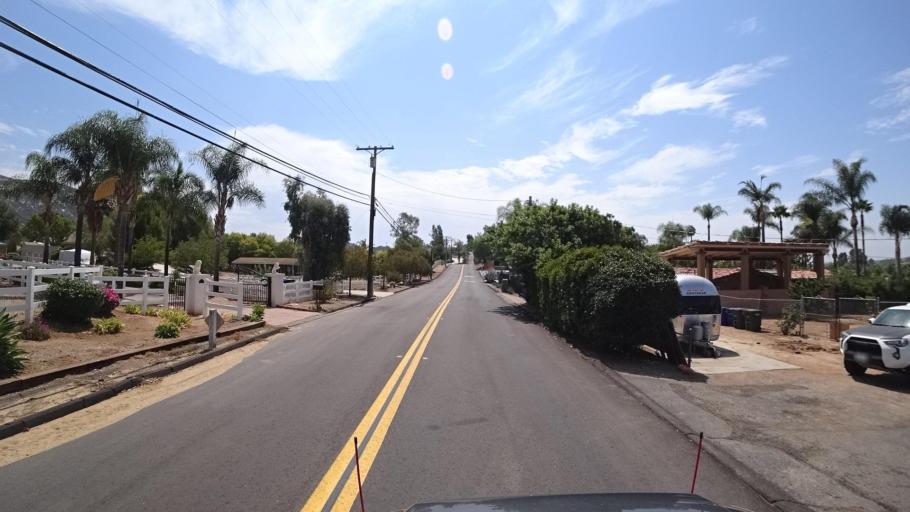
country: US
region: California
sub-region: San Diego County
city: Hidden Meadows
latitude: 33.1767
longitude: -117.0841
